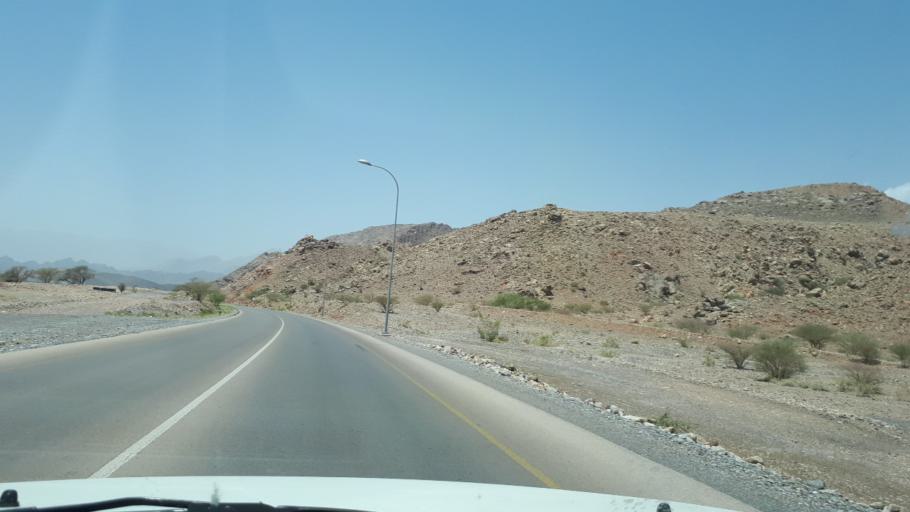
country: OM
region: Muhafazat ad Dakhiliyah
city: Bahla'
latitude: 23.0510
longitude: 57.3081
